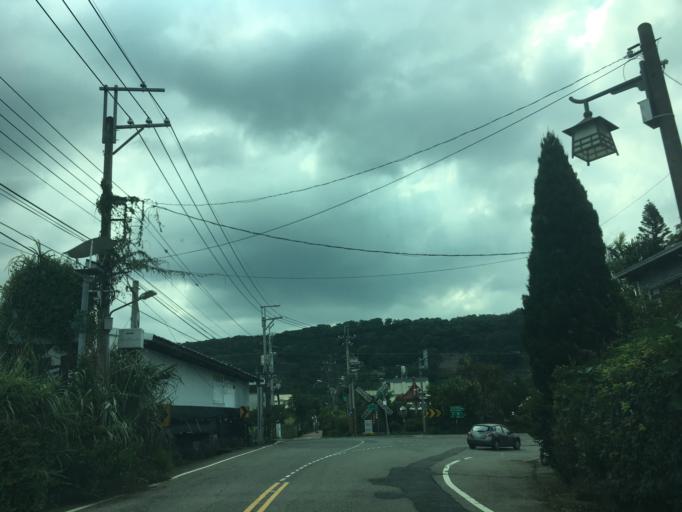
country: TW
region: Taiwan
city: Fengyuan
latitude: 24.2187
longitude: 120.7929
